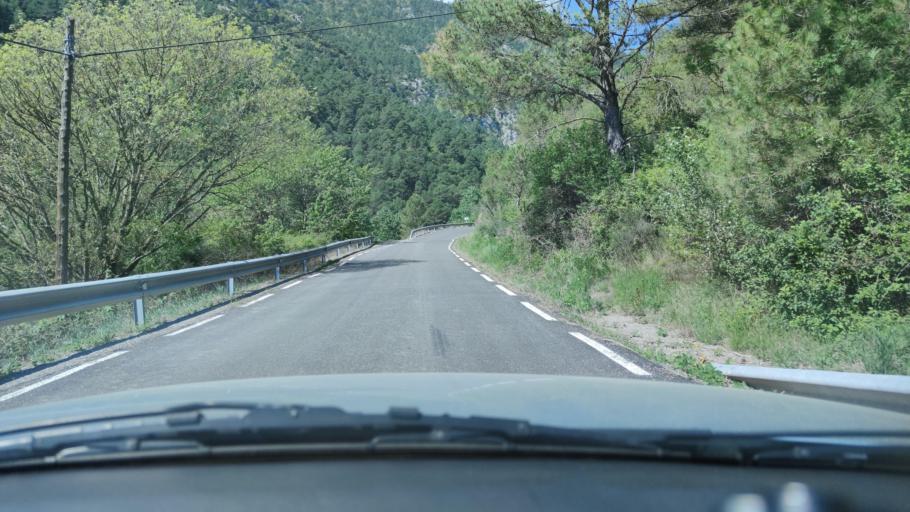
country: ES
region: Catalonia
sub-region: Provincia de Lleida
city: Coll de Nargo
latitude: 42.2912
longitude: 1.3322
